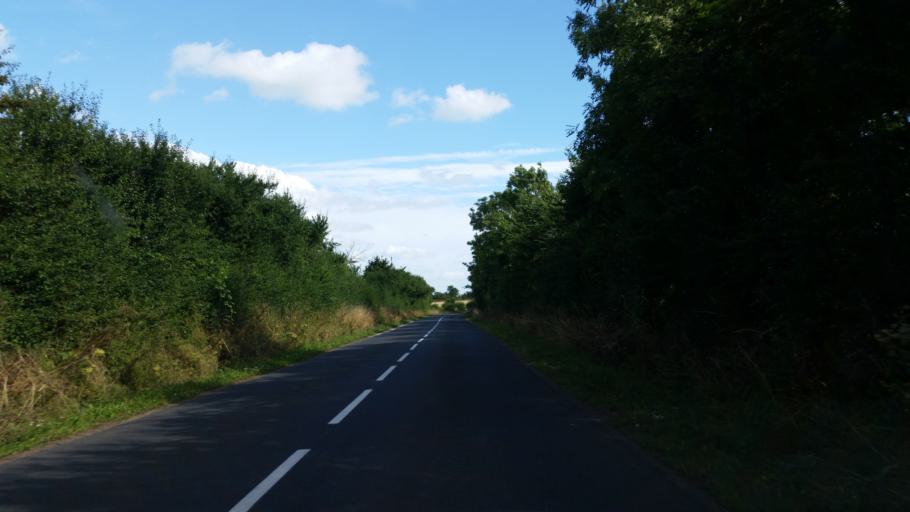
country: FR
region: Lower Normandy
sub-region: Departement de la Manche
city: Sainte-Mere-Eglise
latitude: 49.4531
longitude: -1.2671
